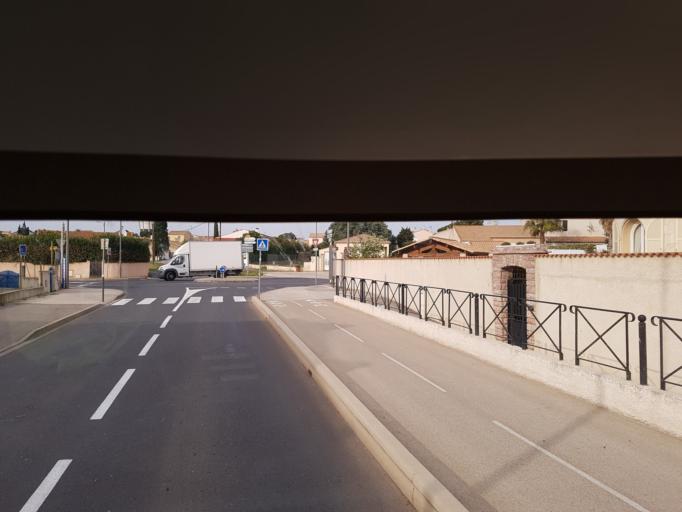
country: FR
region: Languedoc-Roussillon
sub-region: Departement de l'Herault
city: Marseillan
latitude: 43.3601
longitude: 3.5243
